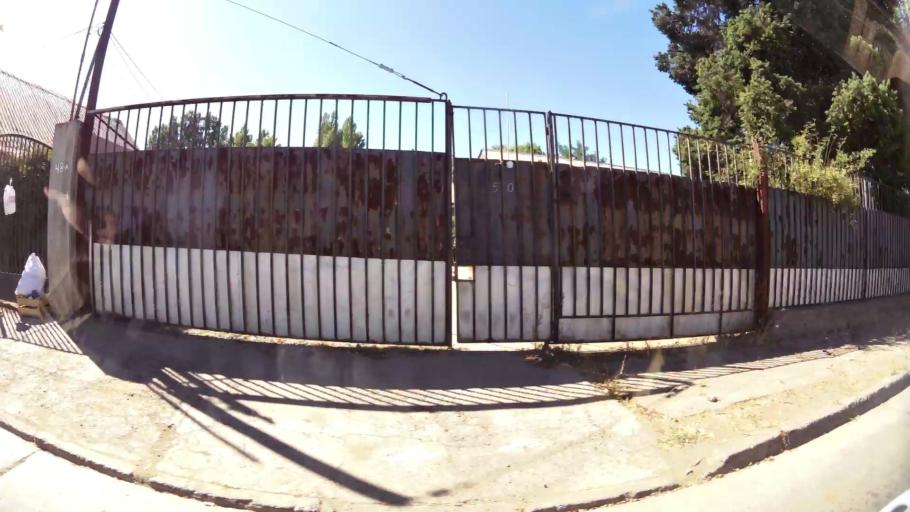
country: CL
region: O'Higgins
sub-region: Provincia de Cachapoal
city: Rancagua
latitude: -34.1710
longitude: -70.7017
